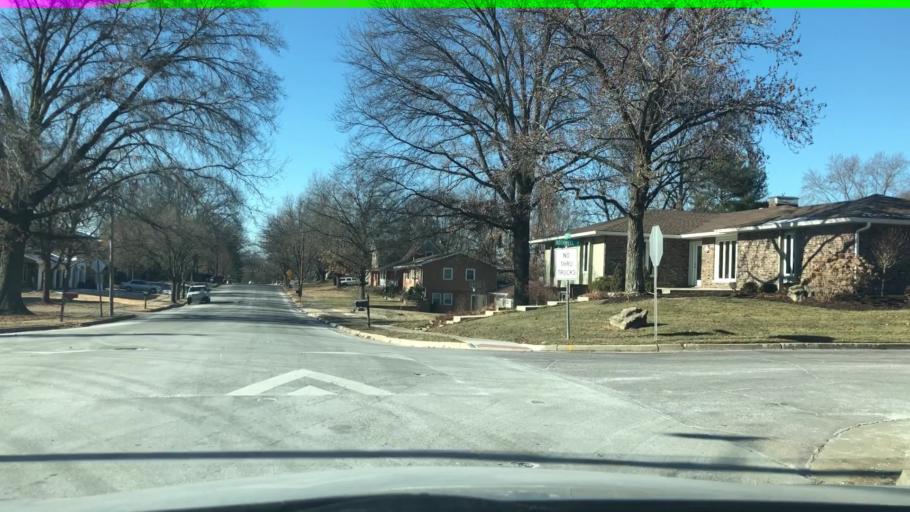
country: US
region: Missouri
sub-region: Boone County
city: Columbia
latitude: 38.9491
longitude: -92.3951
